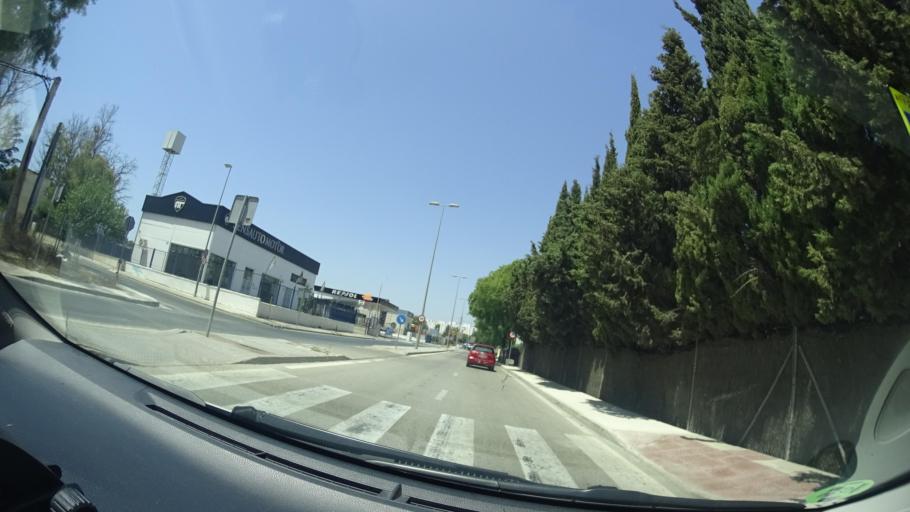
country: ES
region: Andalusia
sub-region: Provincia de Cadiz
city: Jerez de la Frontera
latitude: 36.6706
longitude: -6.1211
